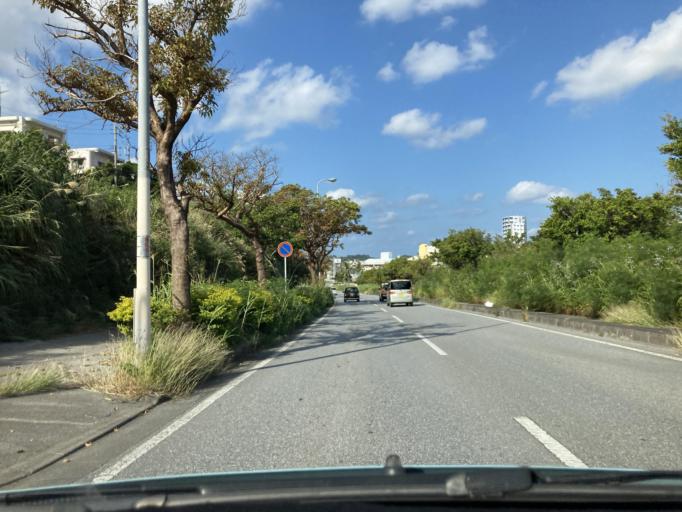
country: JP
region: Okinawa
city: Tomigusuku
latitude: 26.1934
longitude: 127.6979
